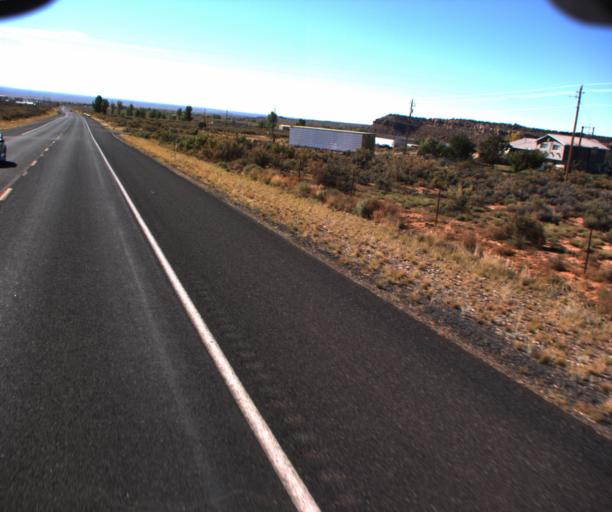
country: US
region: Arizona
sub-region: Coconino County
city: Fredonia
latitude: 36.9837
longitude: -112.5297
